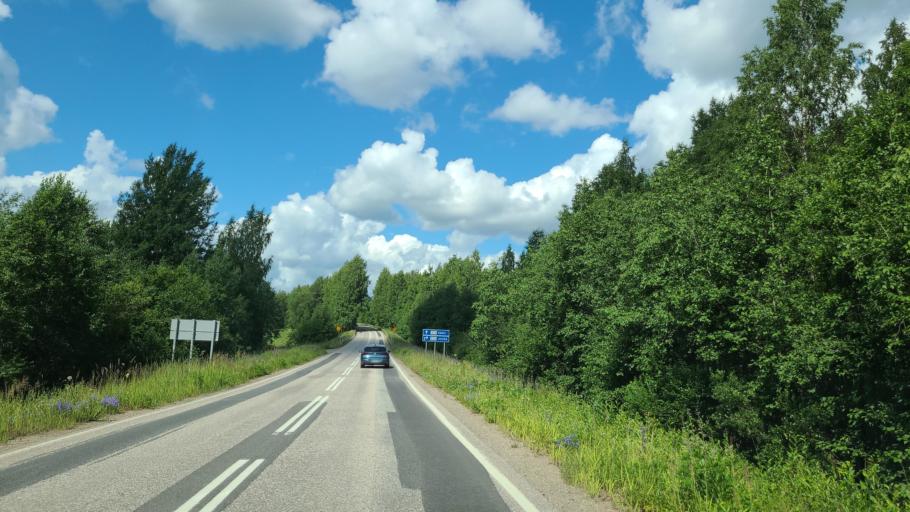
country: FI
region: Northern Savo
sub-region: Koillis-Savo
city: Kaavi
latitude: 62.9215
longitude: 28.6962
